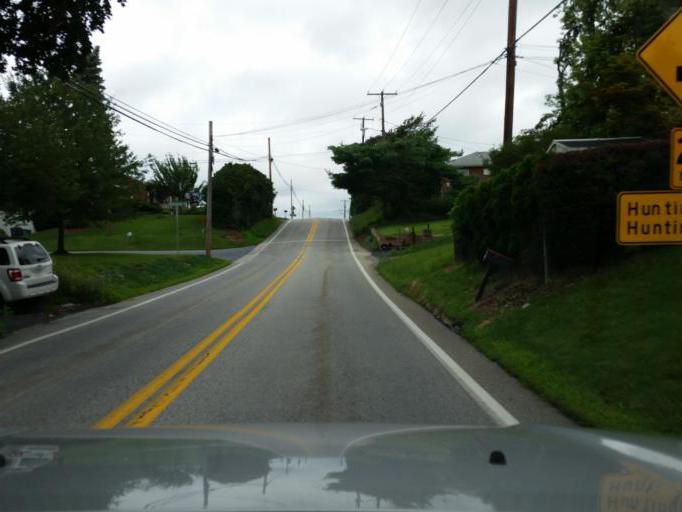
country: US
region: Pennsylvania
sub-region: Dauphin County
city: Rutherford
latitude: 40.2658
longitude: -76.7824
